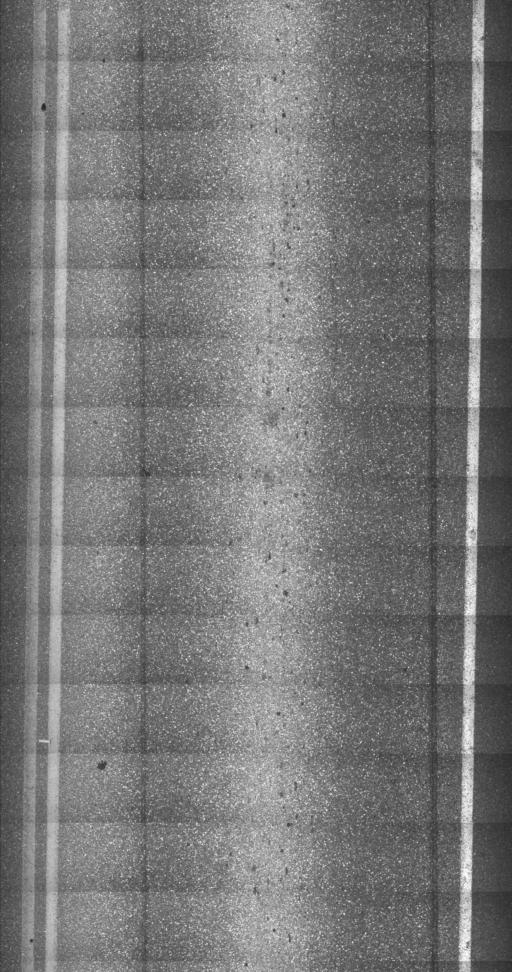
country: US
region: Vermont
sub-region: Lamoille County
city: Morristown
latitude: 44.4735
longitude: -72.7110
